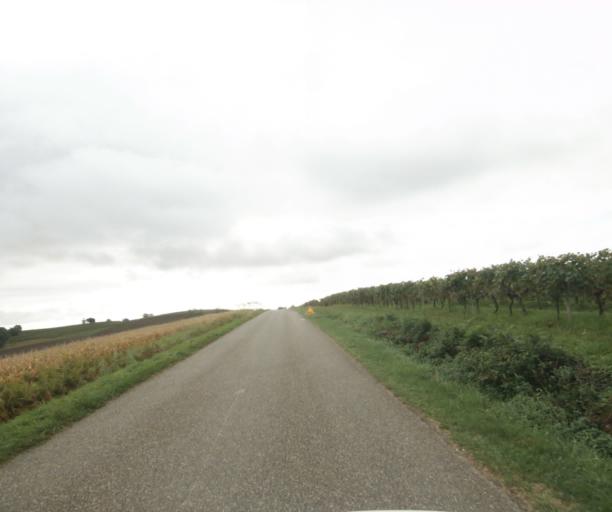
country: FR
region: Midi-Pyrenees
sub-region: Departement du Gers
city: Nogaro
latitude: 43.8310
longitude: -0.0422
